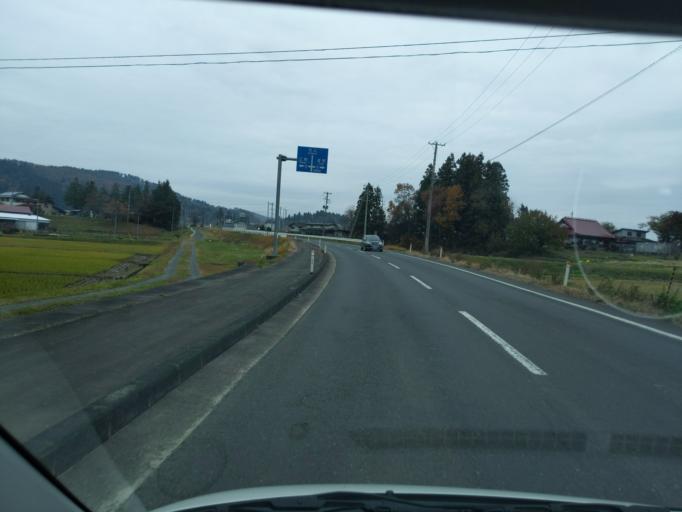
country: JP
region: Iwate
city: Mizusawa
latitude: 39.2174
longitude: 141.2257
